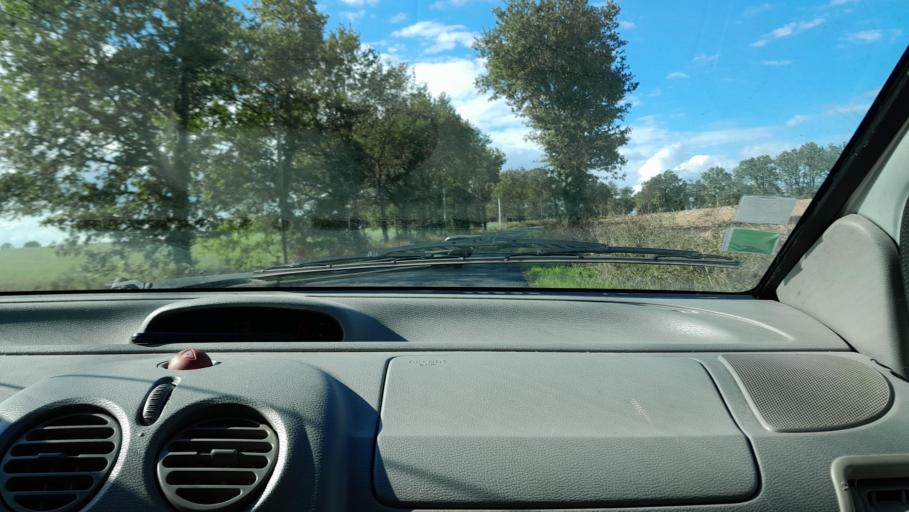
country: FR
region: Pays de la Loire
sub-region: Departement de la Mayenne
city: Ahuille
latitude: 48.0227
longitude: -0.8835
